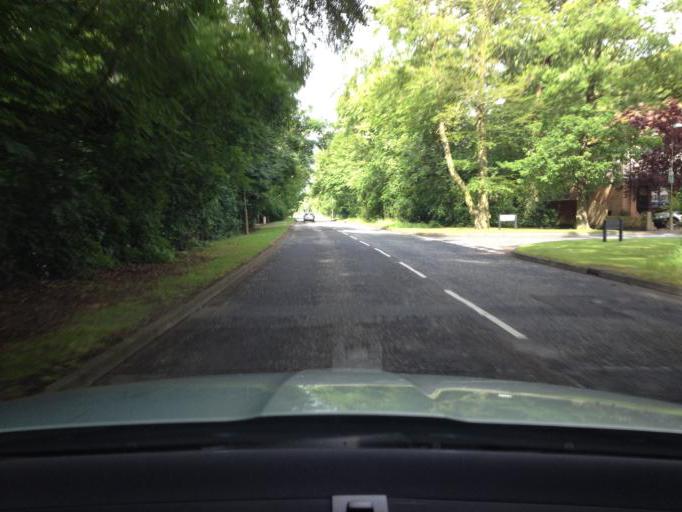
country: GB
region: Scotland
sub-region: West Lothian
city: Livingston
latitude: 55.8660
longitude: -3.5202
